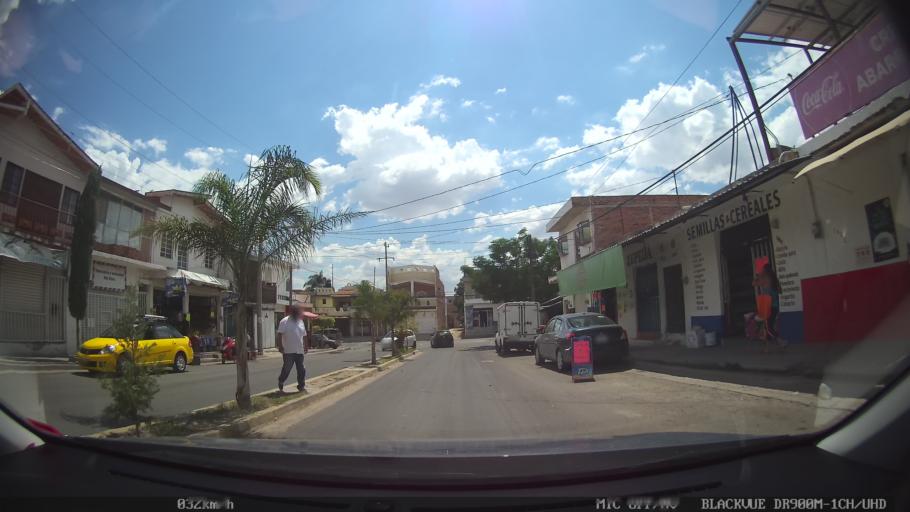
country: MX
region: Jalisco
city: Tlaquepaque
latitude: 20.6691
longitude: -103.2602
